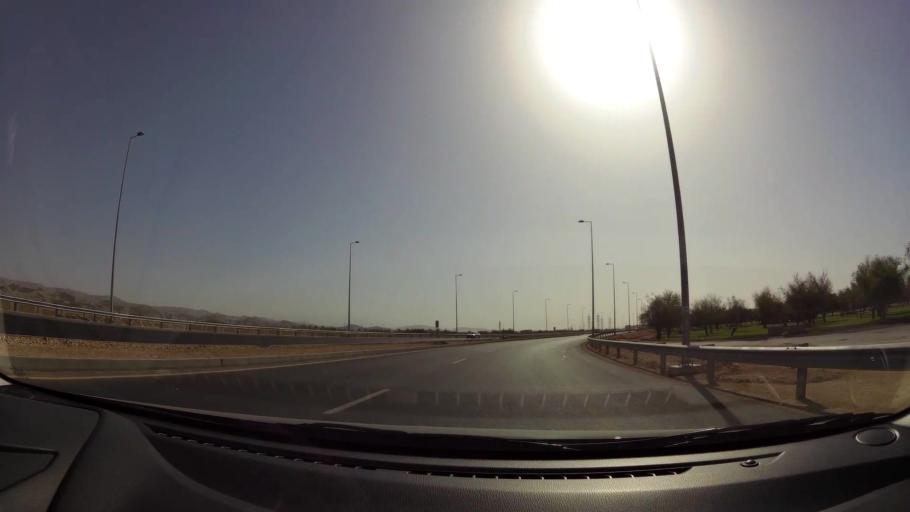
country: OM
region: Muhafazat Masqat
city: As Sib al Jadidah
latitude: 23.5811
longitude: 58.2700
